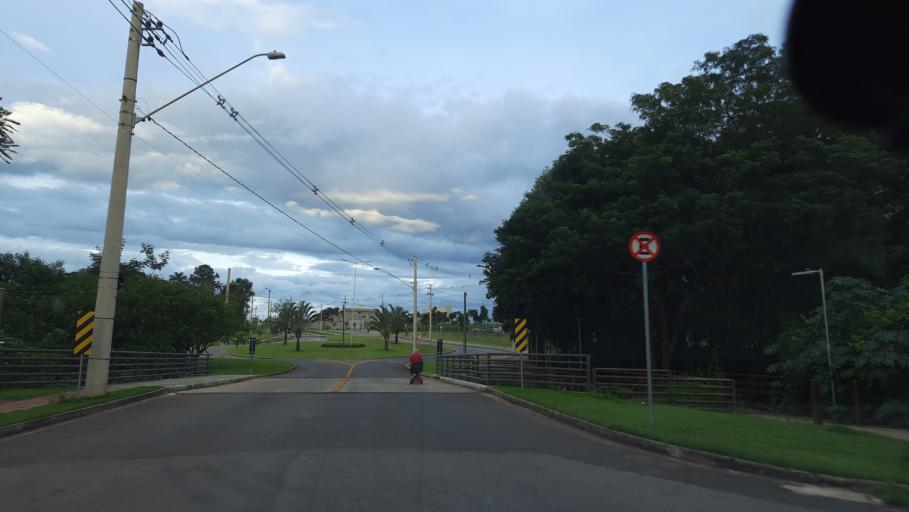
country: BR
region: Sao Paulo
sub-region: Sao Joao Da Boa Vista
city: Sao Joao da Boa Vista
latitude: -21.9637
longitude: -46.7862
